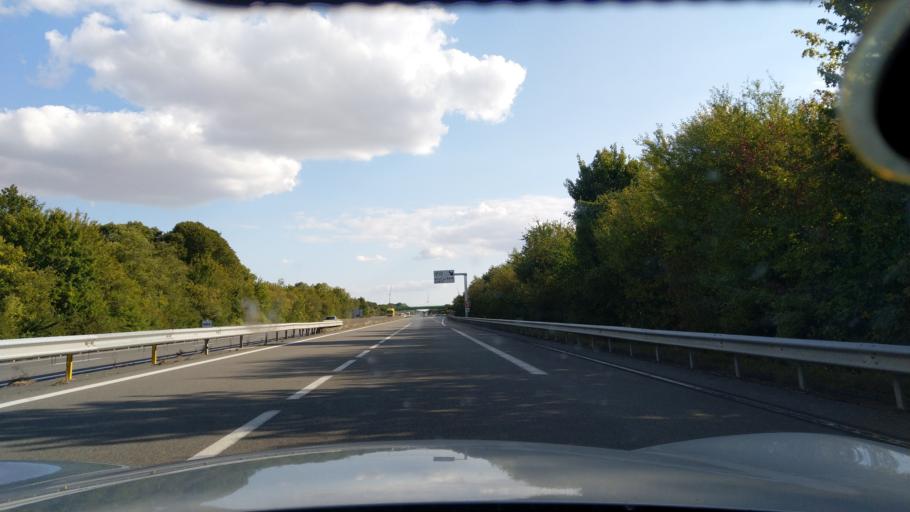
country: FR
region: Picardie
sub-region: Departement de la Somme
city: Conty
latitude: 49.7412
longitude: 2.2329
